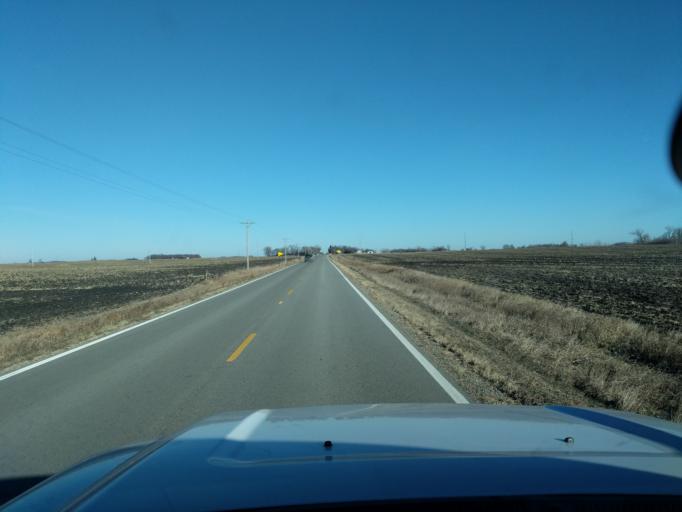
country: US
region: Minnesota
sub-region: Yellow Medicine County
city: Granite Falls
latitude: 44.7848
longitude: -95.4017
